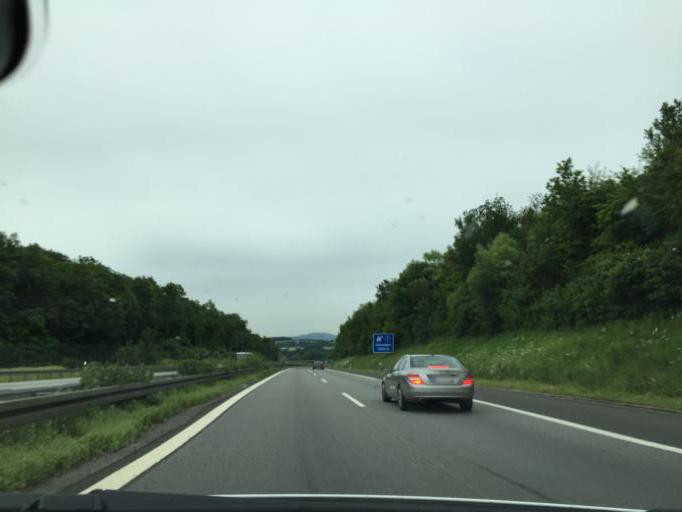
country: DE
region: Bavaria
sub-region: Regierungsbezirk Unterfranken
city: Schonungen
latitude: 50.0266
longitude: 10.3108
